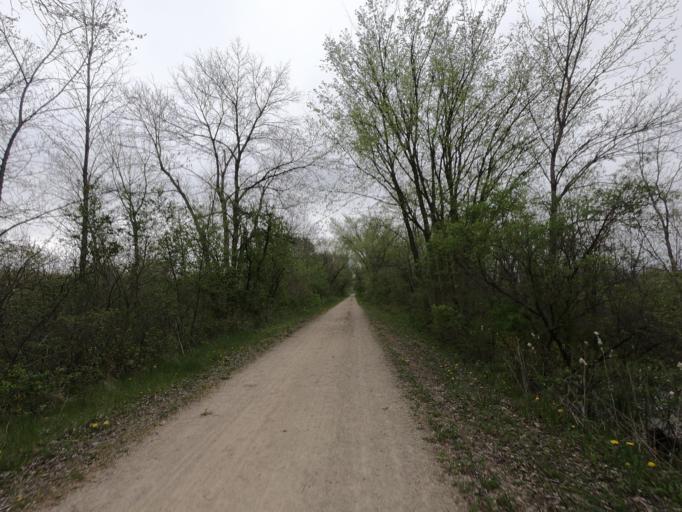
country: US
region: Wisconsin
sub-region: Jefferson County
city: Johnson Creek
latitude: 43.0290
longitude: -88.7420
